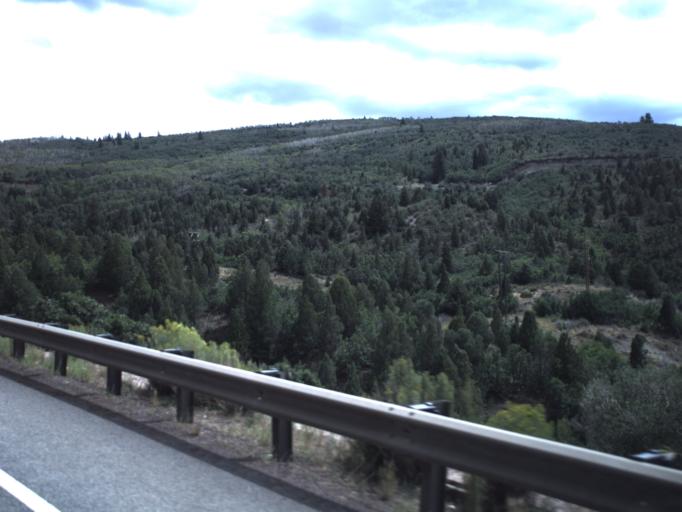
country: US
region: Utah
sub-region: Carbon County
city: Helper
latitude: 39.9350
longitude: -111.1311
